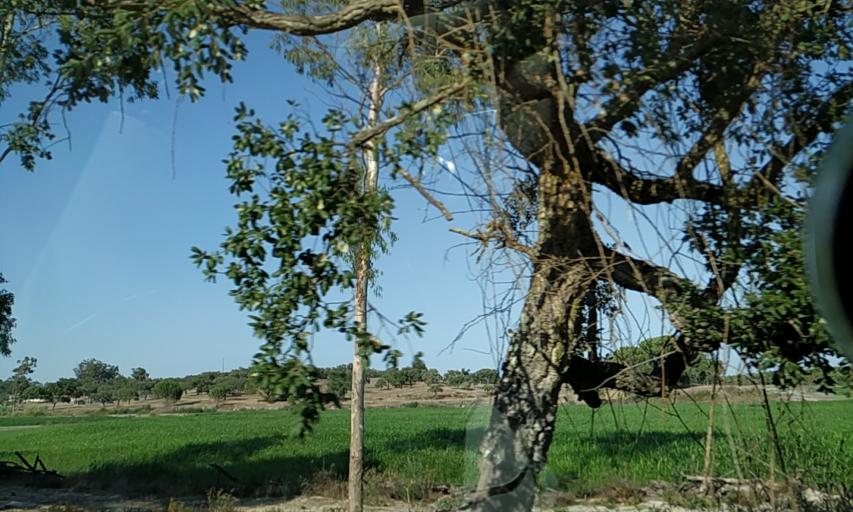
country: PT
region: Santarem
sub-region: Coruche
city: Coruche
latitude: 38.9962
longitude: -8.5556
